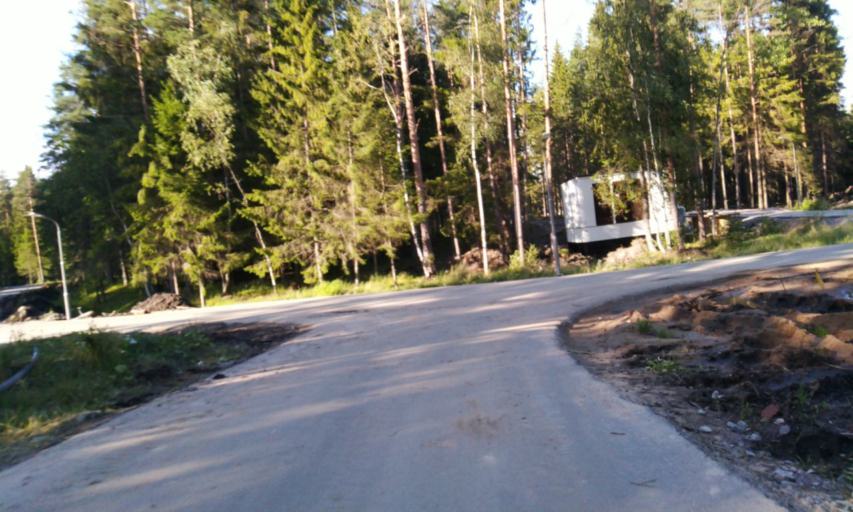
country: RU
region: Leningrad
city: Toksovo
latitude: 60.1295
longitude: 30.4585
